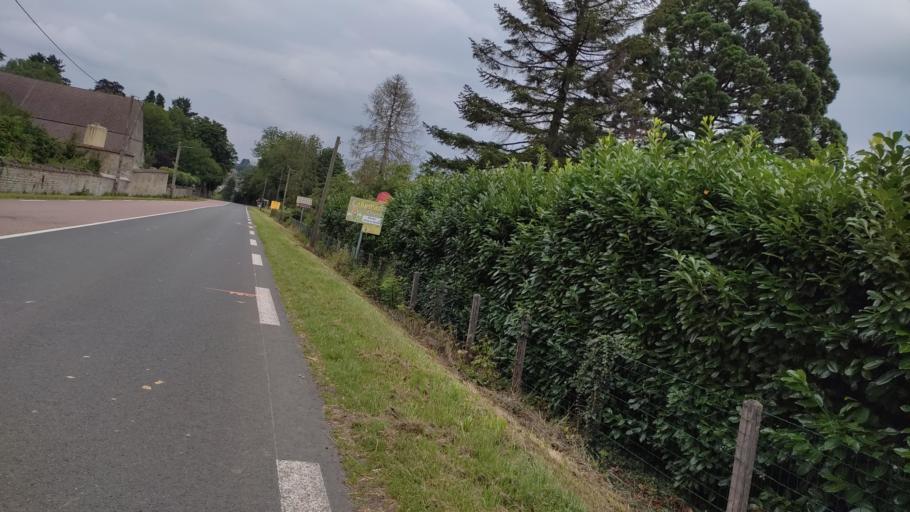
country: FR
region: Bourgogne
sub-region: Departement de la Nievre
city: Chatillon-en-Bazois
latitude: 47.0478
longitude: 3.6487
